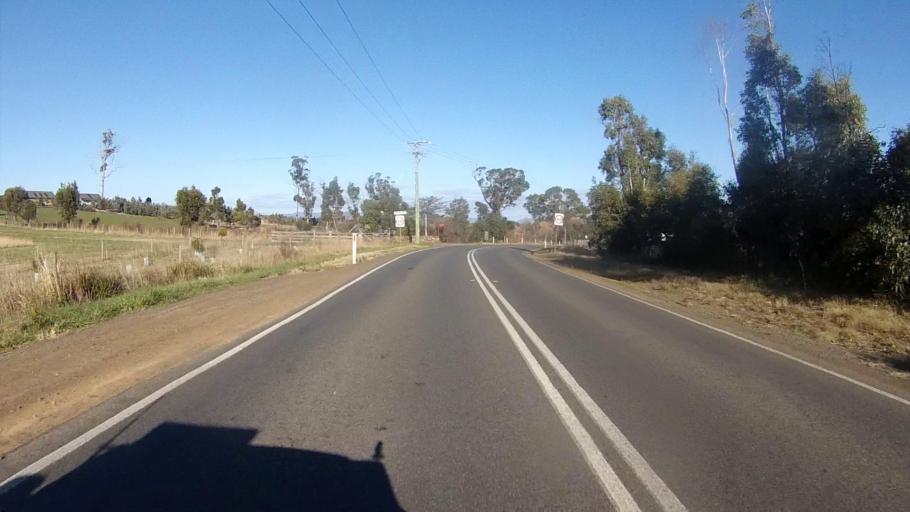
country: AU
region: Tasmania
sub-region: Sorell
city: Sorell
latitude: -42.8749
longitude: 147.8243
